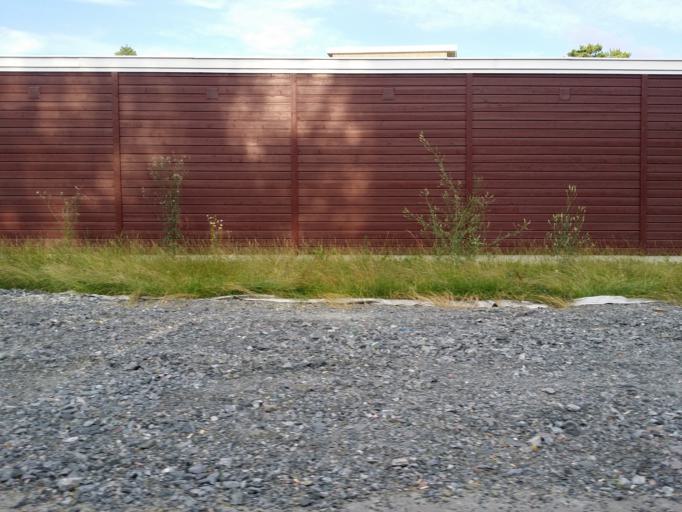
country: NO
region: Akershus
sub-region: Oppegard
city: Kolbotn
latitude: 59.8979
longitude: 10.8525
